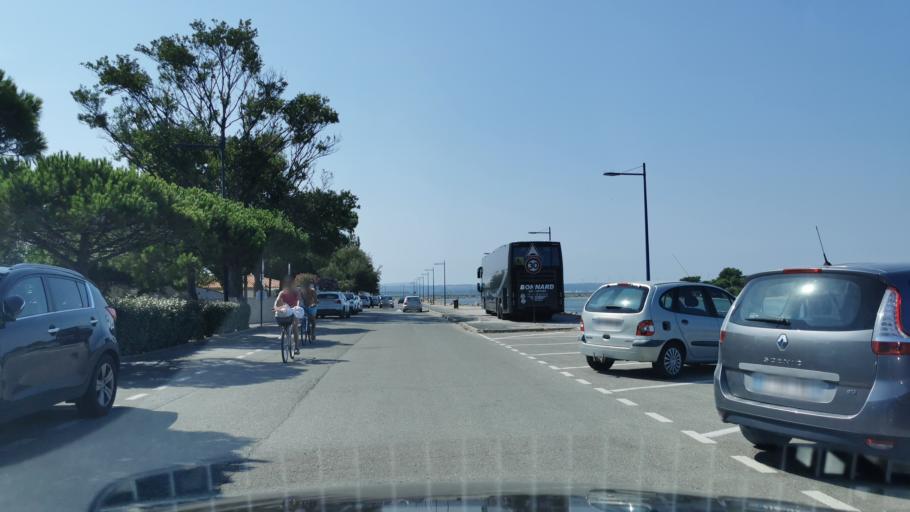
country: FR
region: Languedoc-Roussillon
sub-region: Departement de l'Aude
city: Leucate
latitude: 42.9355
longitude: 3.0316
